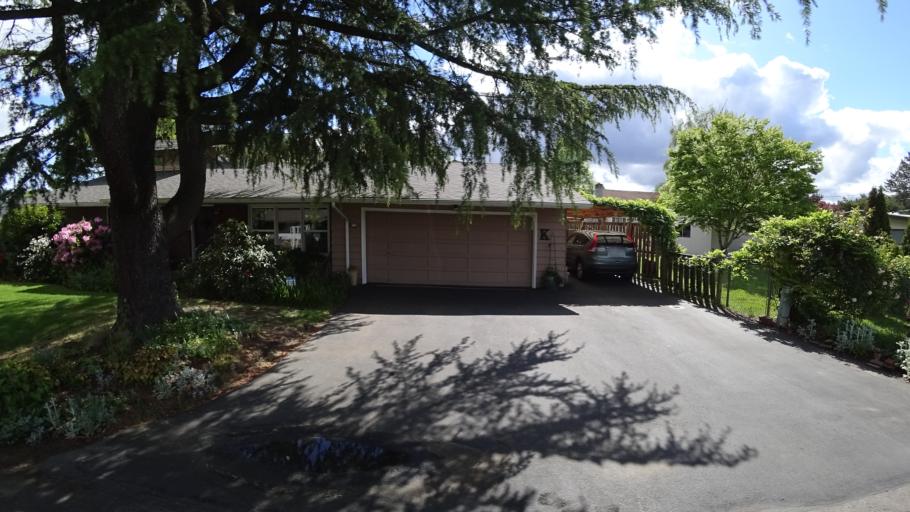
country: US
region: Oregon
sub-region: Washington County
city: Metzger
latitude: 45.4452
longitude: -122.7489
